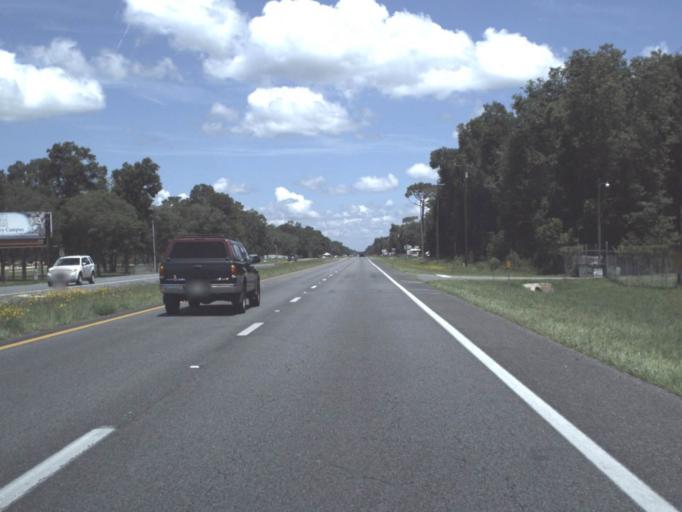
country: US
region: Florida
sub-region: Levy County
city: Manatee Road
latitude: 29.5505
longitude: -82.9000
